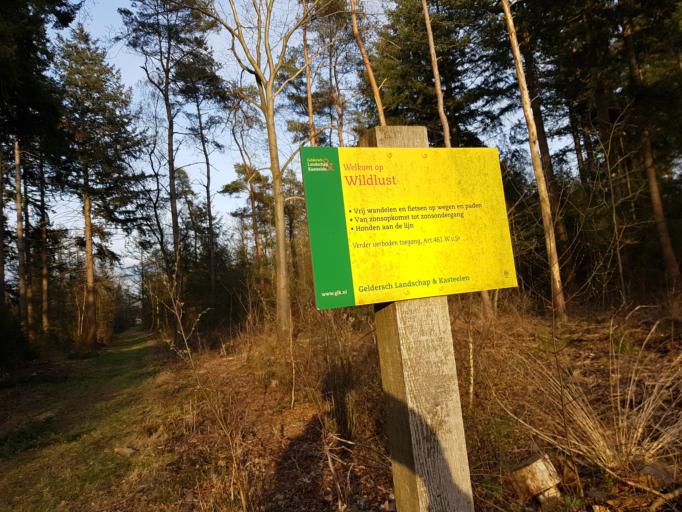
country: NL
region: Gelderland
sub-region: Gemeente Epe
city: Emst
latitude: 52.3152
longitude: 5.9312
